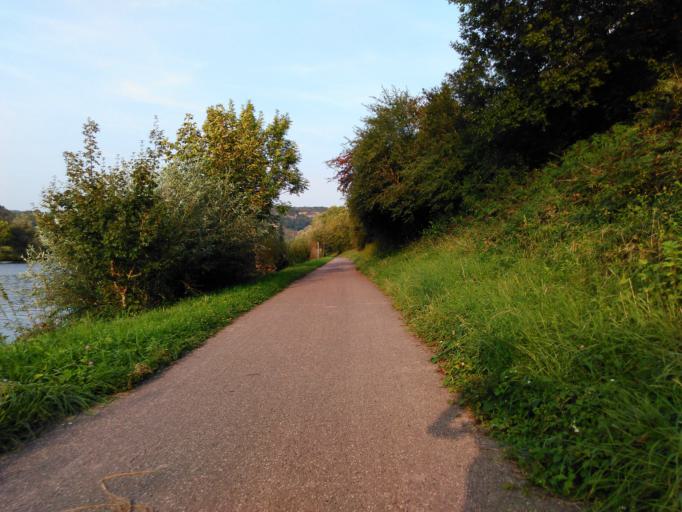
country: LU
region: Grevenmacher
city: Wasserbillig
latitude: 49.7108
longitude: 6.5147
